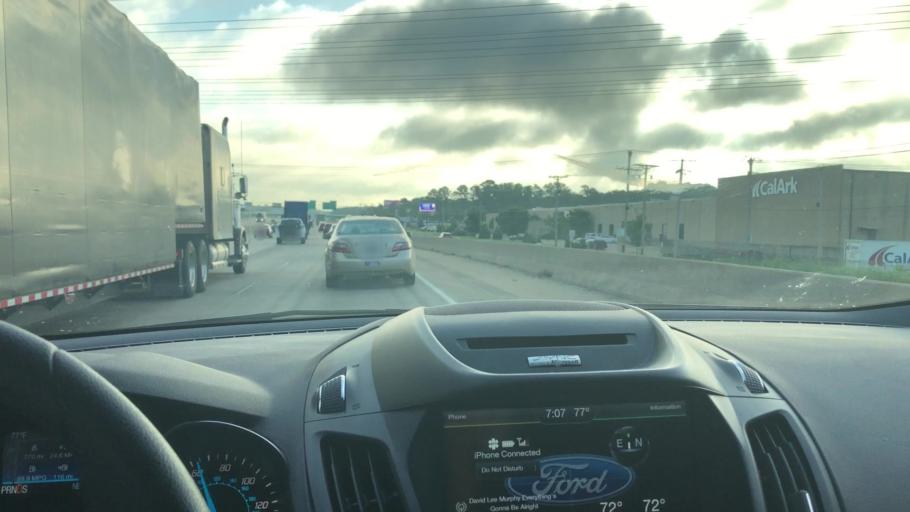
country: US
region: Arkansas
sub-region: Pulaski County
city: Alexander
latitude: 34.6501
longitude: -92.4161
